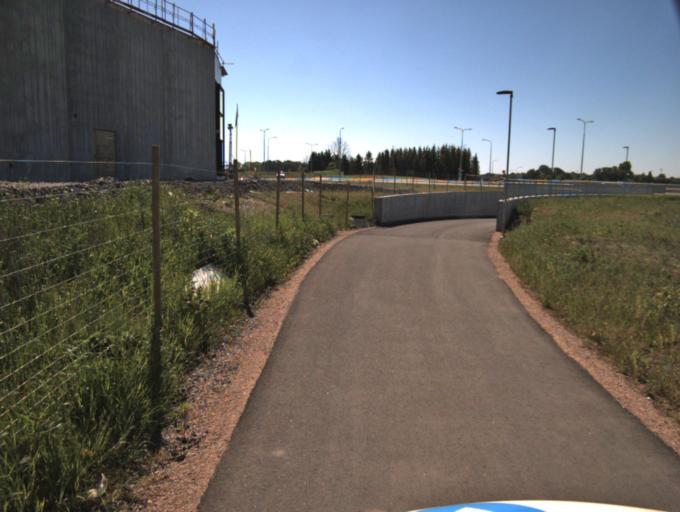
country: SE
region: Skane
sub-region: Kristianstads Kommun
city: Kristianstad
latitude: 56.0245
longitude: 14.1922
